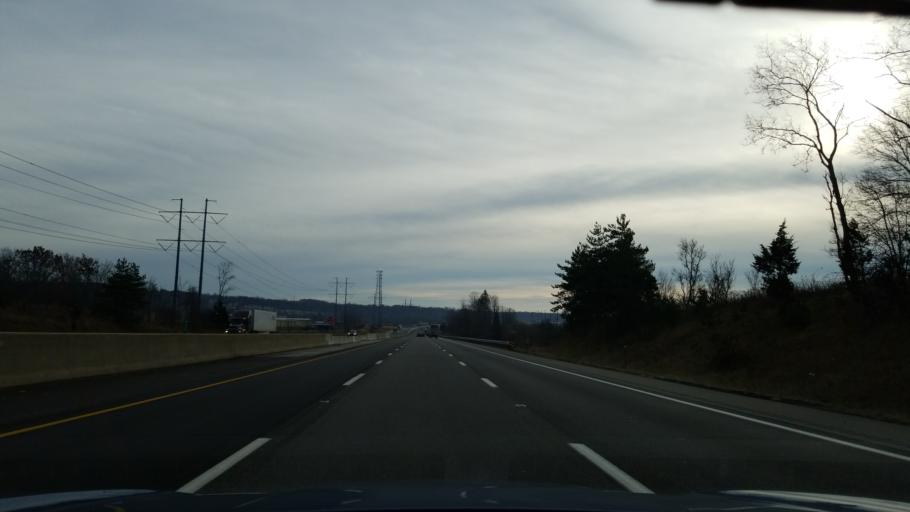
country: US
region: Ohio
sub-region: Cuyahoga County
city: North Royalton
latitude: 41.3173
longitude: -81.7705
